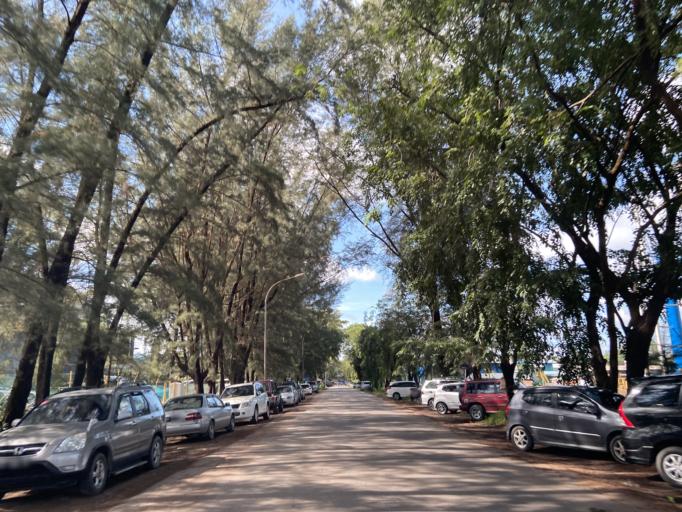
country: SG
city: Singapore
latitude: 1.1722
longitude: 104.0073
